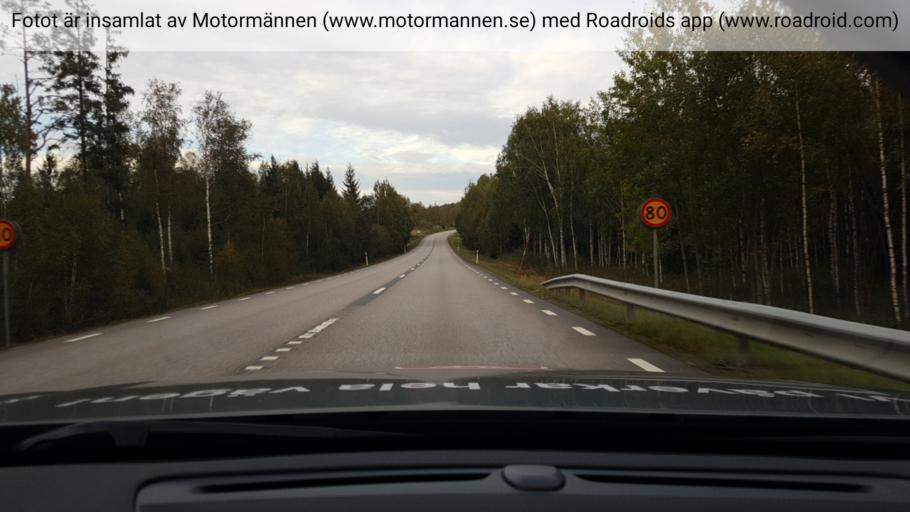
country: SE
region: Vaestra Goetaland
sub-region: Bengtsfors Kommun
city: Bengtsfors
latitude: 59.0248
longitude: 12.2802
